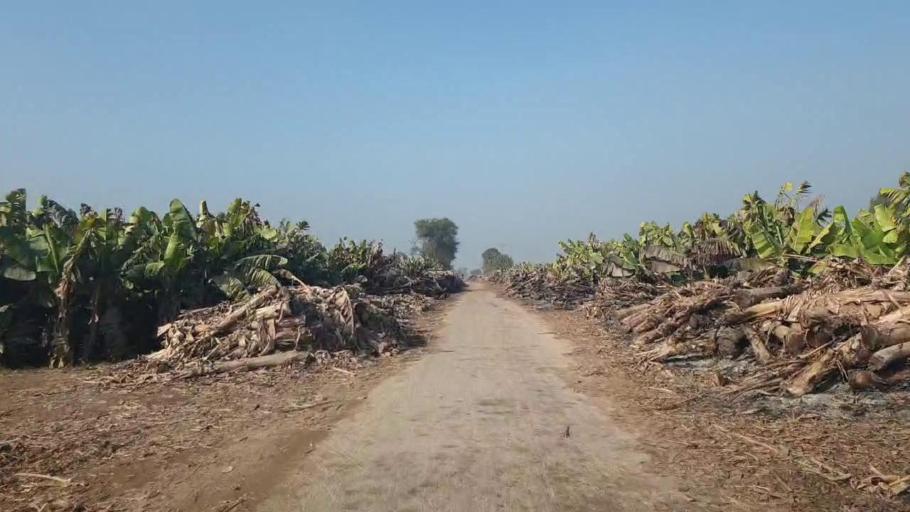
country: PK
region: Sindh
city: Shahdadpur
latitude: 25.9437
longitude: 68.5976
